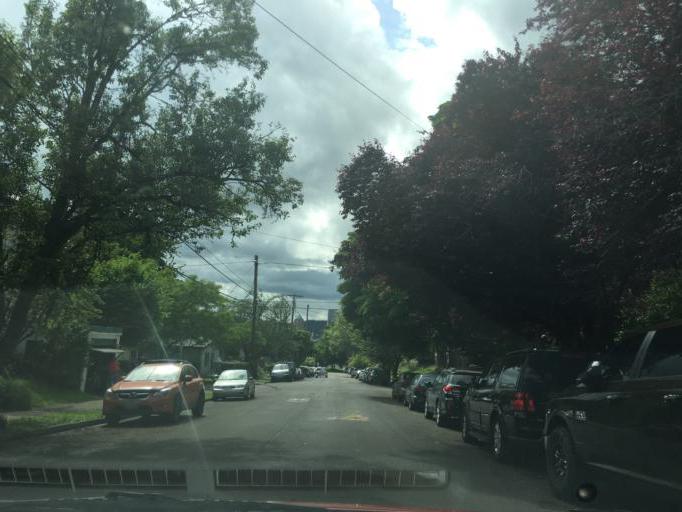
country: US
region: Oregon
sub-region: Multnomah County
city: Portland
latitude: 45.5143
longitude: -122.6500
